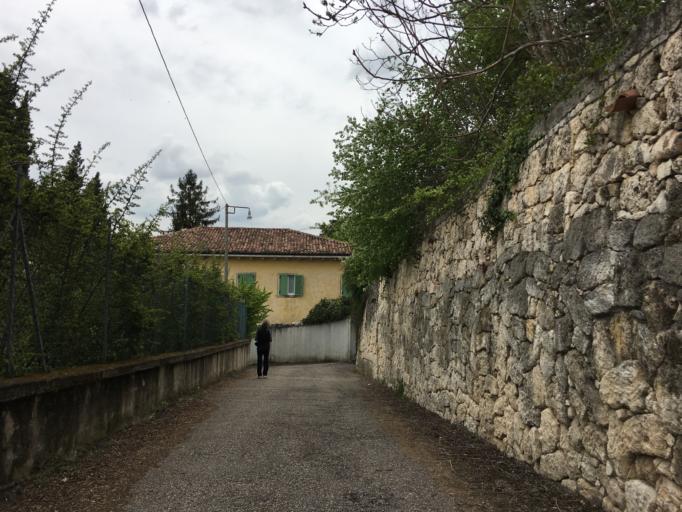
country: IT
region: Veneto
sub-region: Provincia di Verona
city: Verona
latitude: 45.4533
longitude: 10.9964
